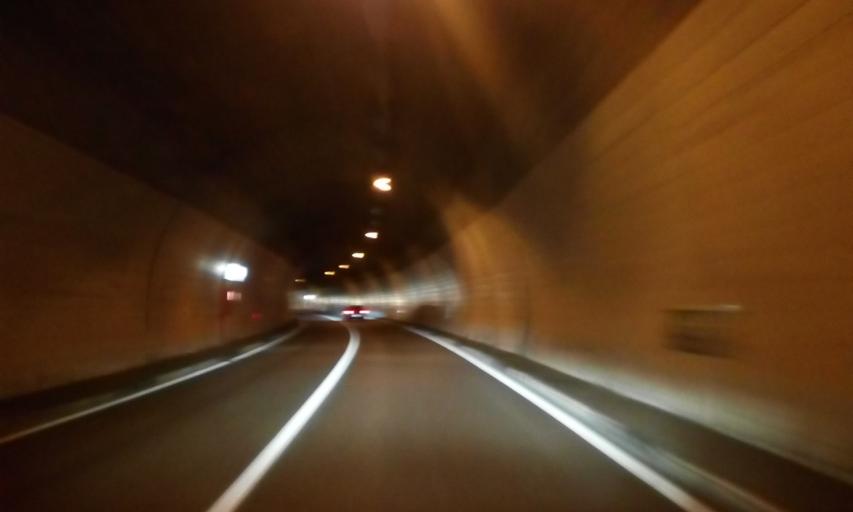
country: CH
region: Grisons
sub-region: Albula District
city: Tiefencastel
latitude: 46.6768
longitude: 9.5435
